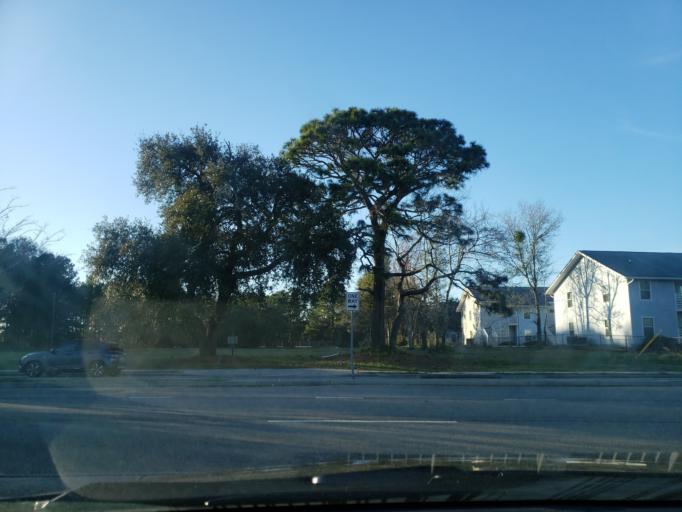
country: US
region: Georgia
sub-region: Chatham County
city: Montgomery
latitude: 31.9974
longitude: -81.1480
